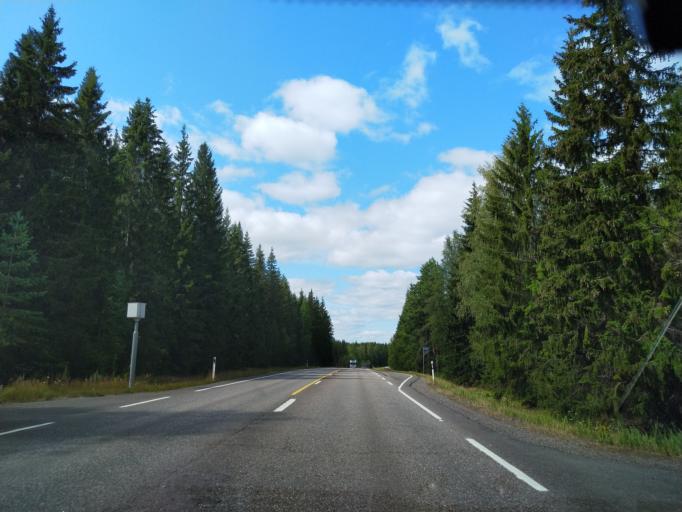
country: FI
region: Haeme
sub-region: Haemeenlinna
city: Renko
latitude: 60.7661
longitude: 24.2509
